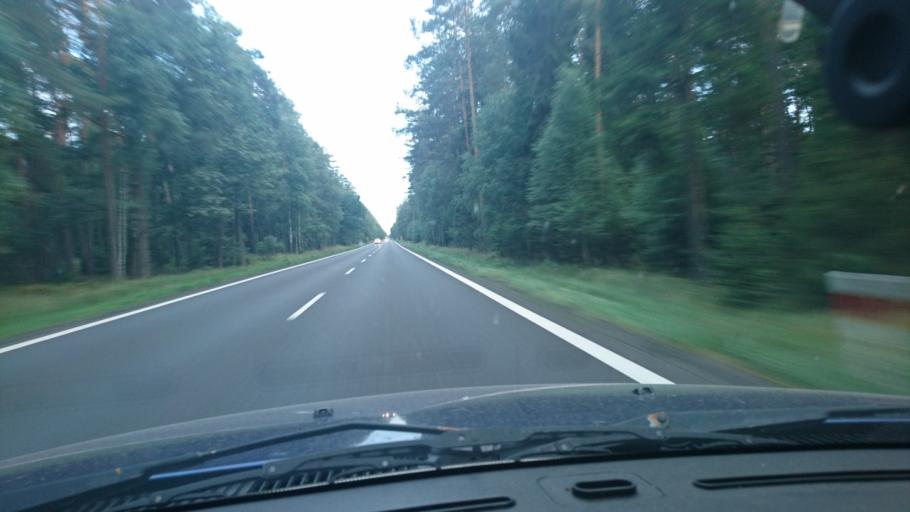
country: PL
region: Silesian Voivodeship
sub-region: Powiat tarnogorski
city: Tworog
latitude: 50.5756
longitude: 18.7094
